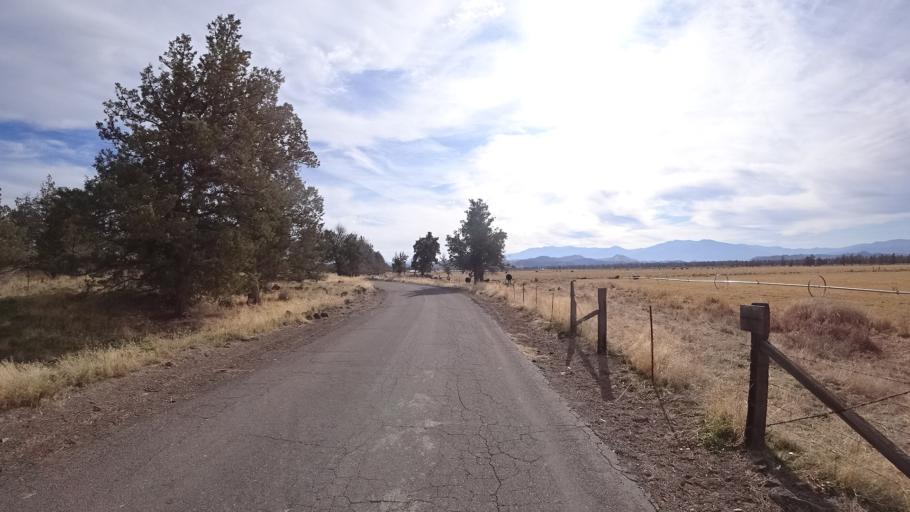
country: US
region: California
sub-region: Siskiyou County
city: Montague
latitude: 41.6054
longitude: -122.4051
